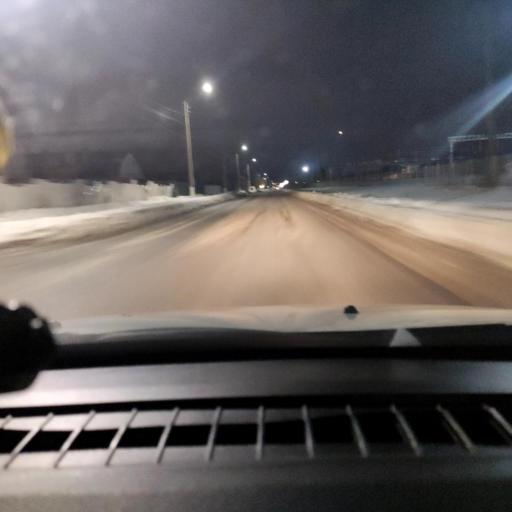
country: RU
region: Samara
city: Chapayevsk
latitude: 52.9762
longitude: 49.7002
